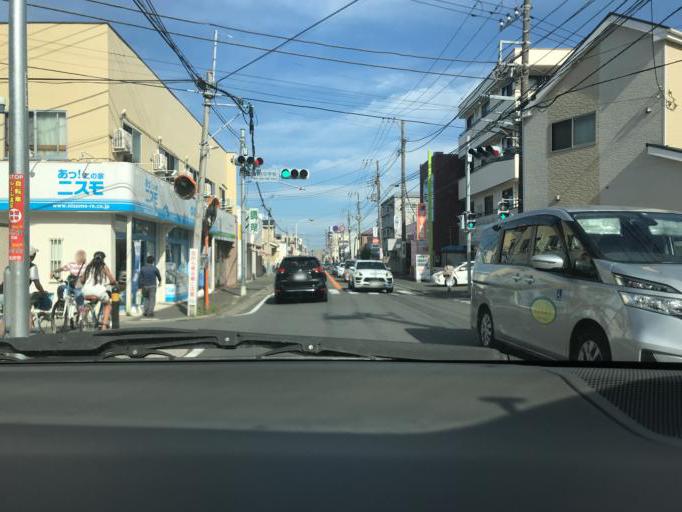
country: JP
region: Kanagawa
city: Fujisawa
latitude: 35.3419
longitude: 139.4563
